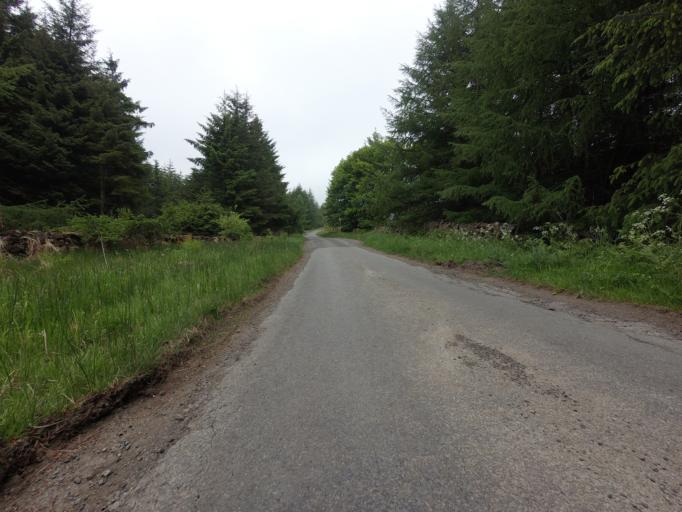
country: GB
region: Scotland
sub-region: Fife
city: Townhill
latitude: 56.1415
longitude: -3.4471
